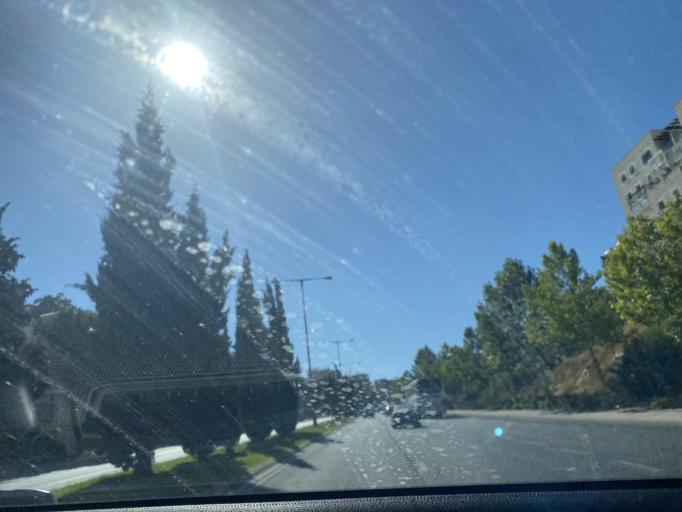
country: PS
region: West Bank
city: Bayt Iksa
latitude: 31.8193
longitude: 35.1930
